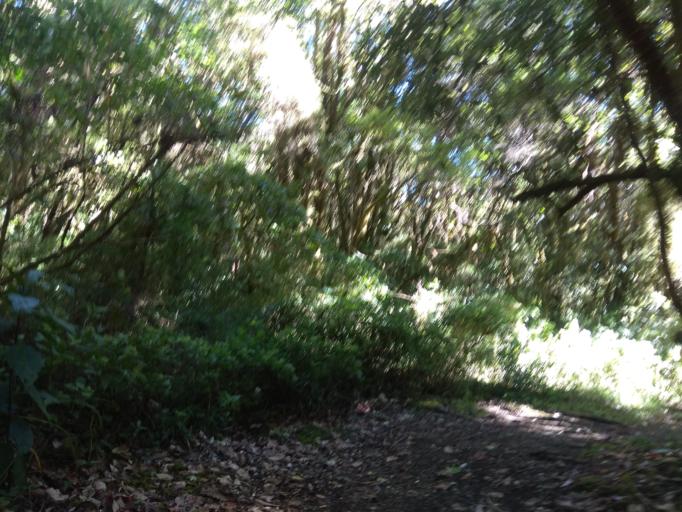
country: CR
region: Heredia
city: Santo Domingo
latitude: 10.1325
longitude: -84.1180
